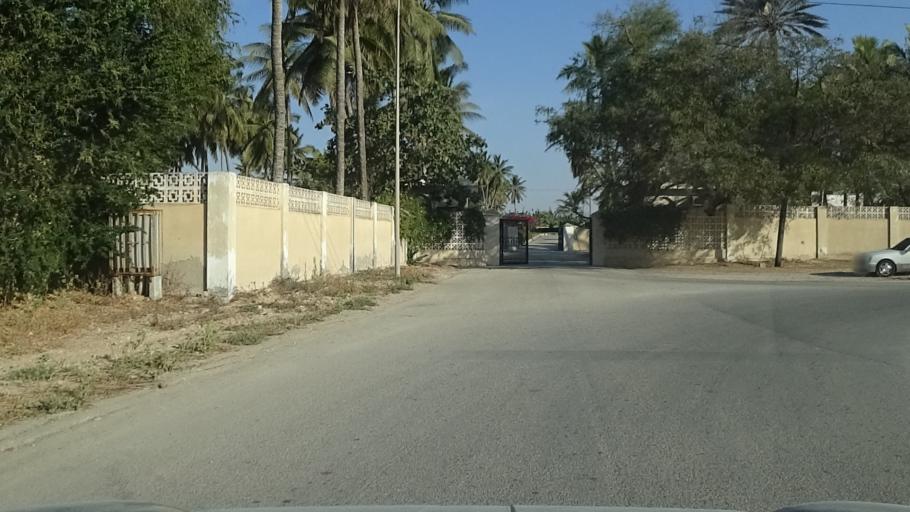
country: OM
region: Zufar
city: Salalah
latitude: 17.0193
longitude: 54.1494
